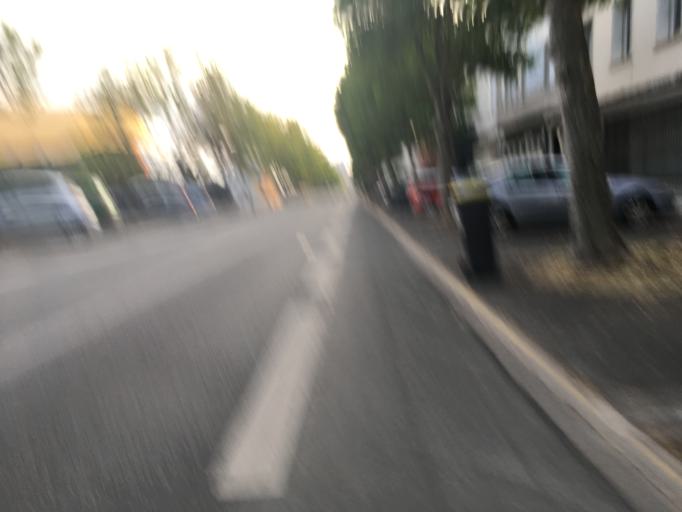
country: FR
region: Poitou-Charentes
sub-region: Departement de la Charente-Maritime
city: Rivedoux-Plage
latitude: 46.1610
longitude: -1.2138
